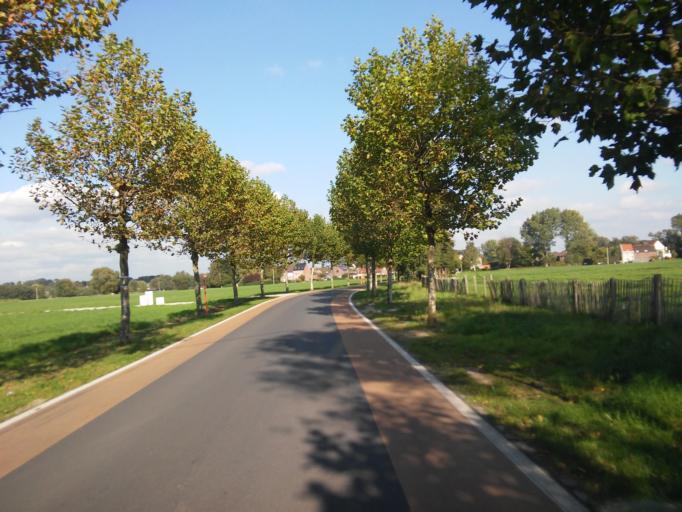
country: BE
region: Flanders
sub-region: Provincie Antwerpen
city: Boom
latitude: 51.0932
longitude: 4.3963
